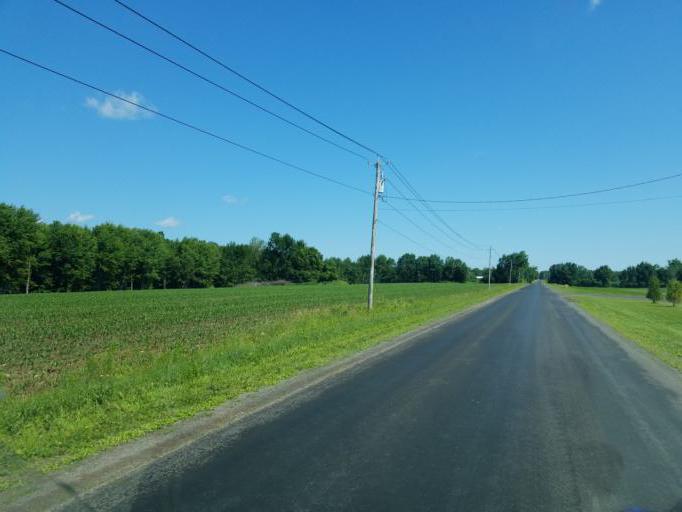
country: US
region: New York
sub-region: Wayne County
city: Wolcott
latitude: 43.1796
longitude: -76.8669
